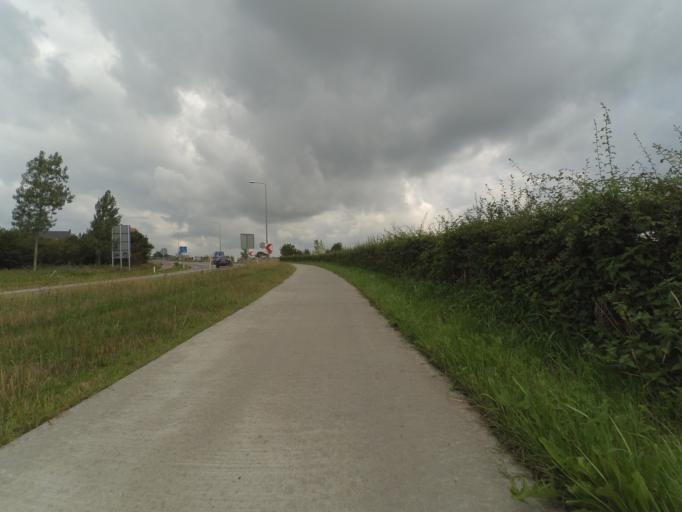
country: BE
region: Flanders
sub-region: Provincie Limburg
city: Maaseik
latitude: 51.0912
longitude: 5.8007
